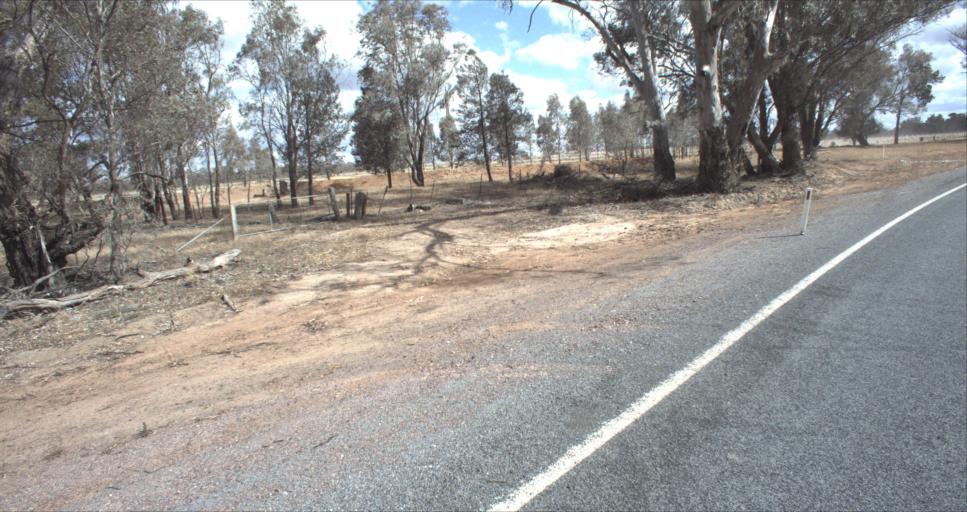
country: AU
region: New South Wales
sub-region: Leeton
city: Leeton
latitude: -34.6432
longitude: 146.3567
